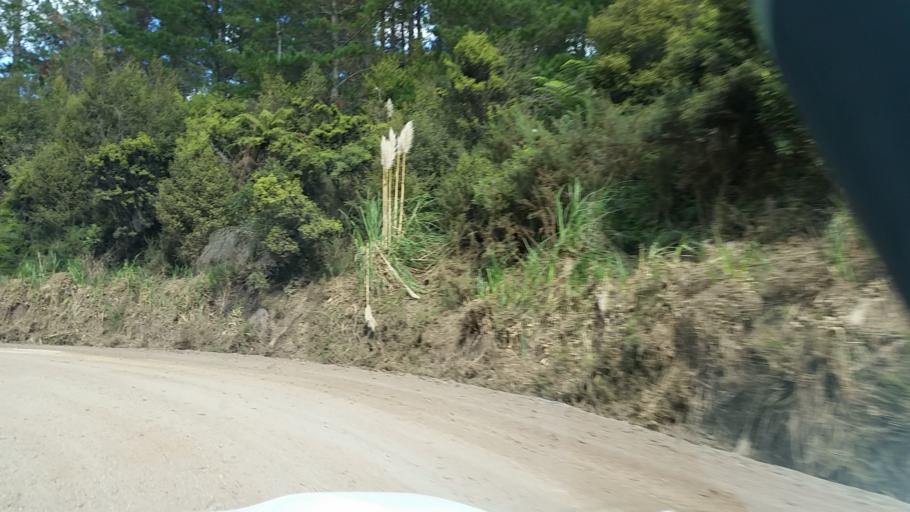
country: NZ
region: Northland
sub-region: Whangarei
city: Whangarei
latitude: -35.5959
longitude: 174.3181
